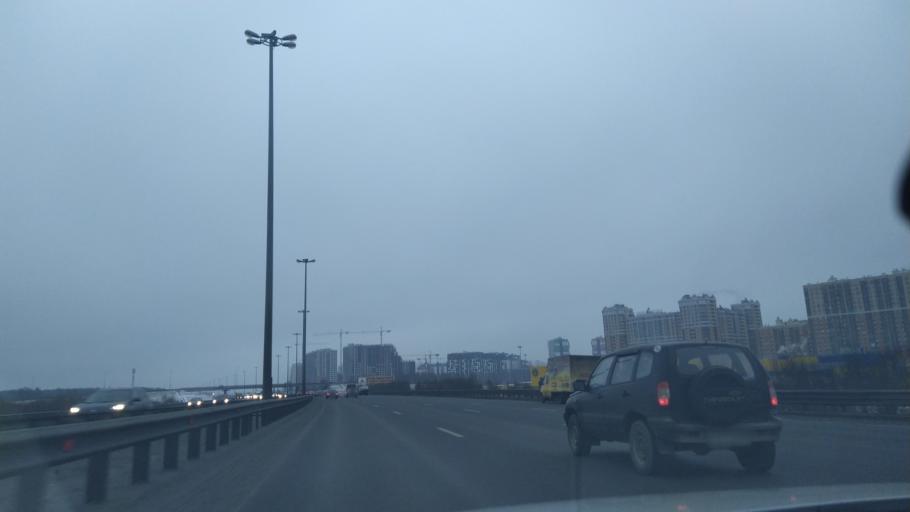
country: RU
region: St.-Petersburg
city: Krasnogvargeisky
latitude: 59.9200
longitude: 30.5263
